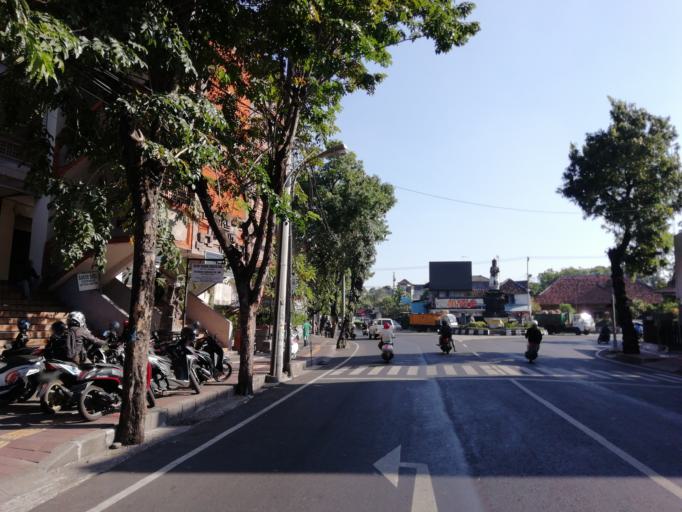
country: ID
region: Bali
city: Denpasar
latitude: -8.6594
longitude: 115.2148
